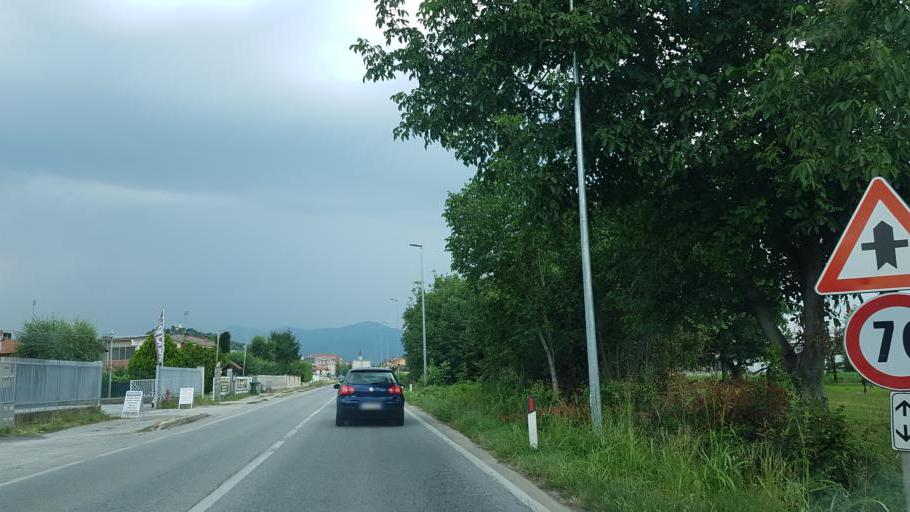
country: IT
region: Piedmont
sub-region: Provincia di Cuneo
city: Caraglio
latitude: 44.4108
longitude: 7.4400
